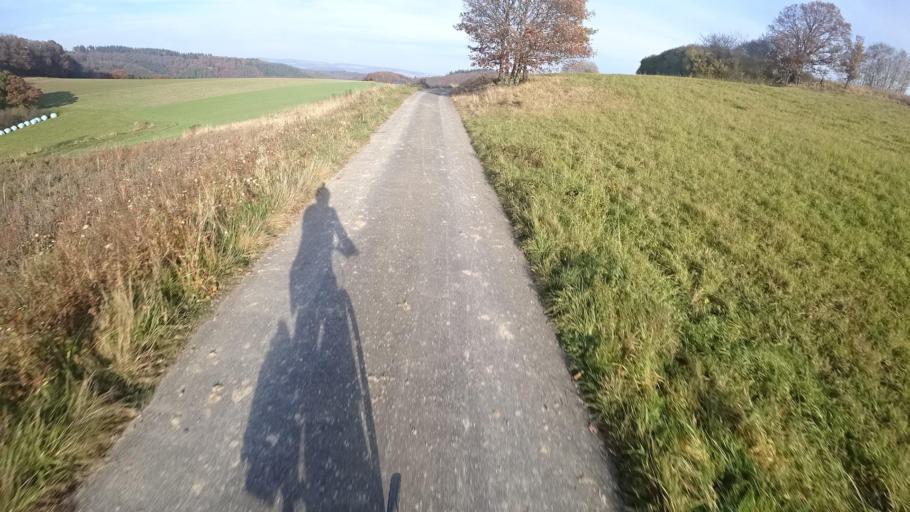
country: DE
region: Rheinland-Pfalz
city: Utzenhain
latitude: 50.1307
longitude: 7.6333
